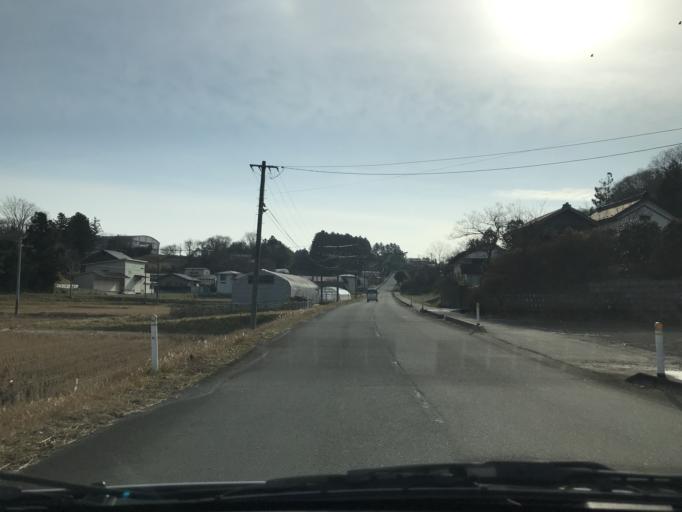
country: JP
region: Miyagi
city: Wakuya
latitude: 38.7039
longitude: 141.1574
